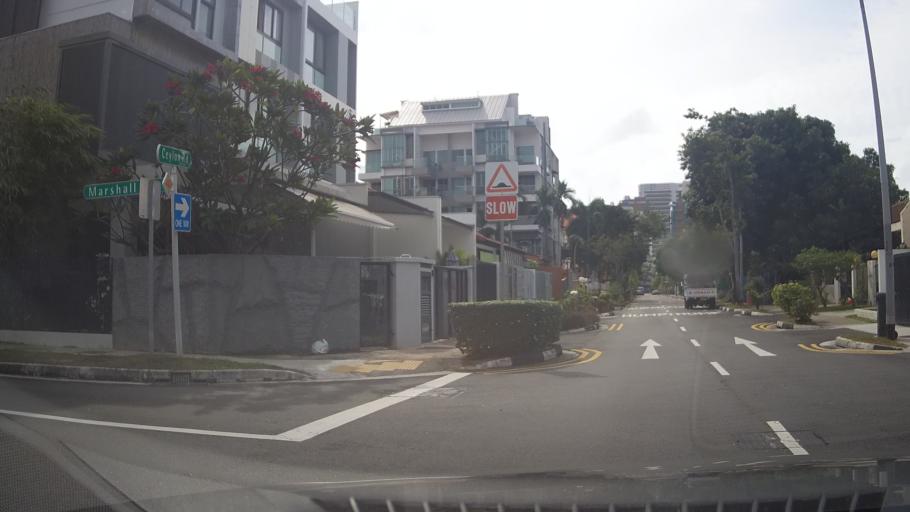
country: SG
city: Singapore
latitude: 1.3075
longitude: 103.9014
